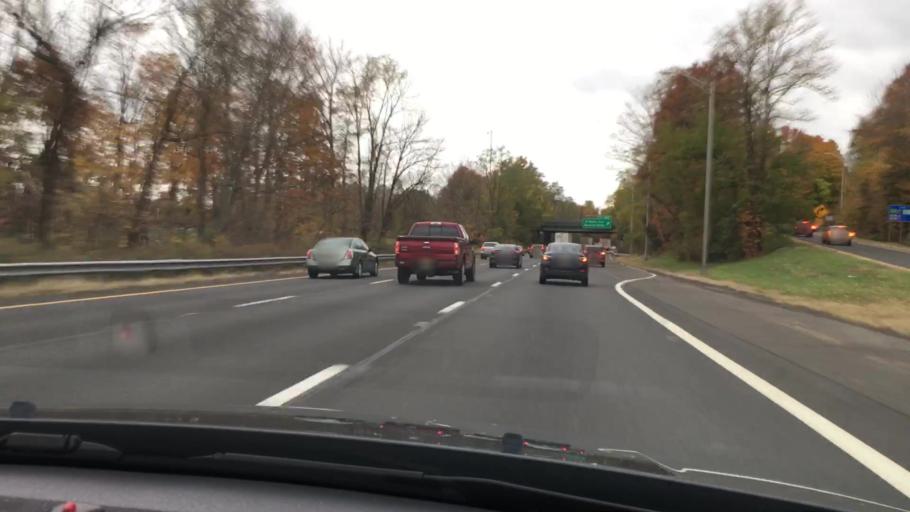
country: US
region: New Jersey
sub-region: Somerset County
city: Bernardsville
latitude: 40.7313
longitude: -74.5384
